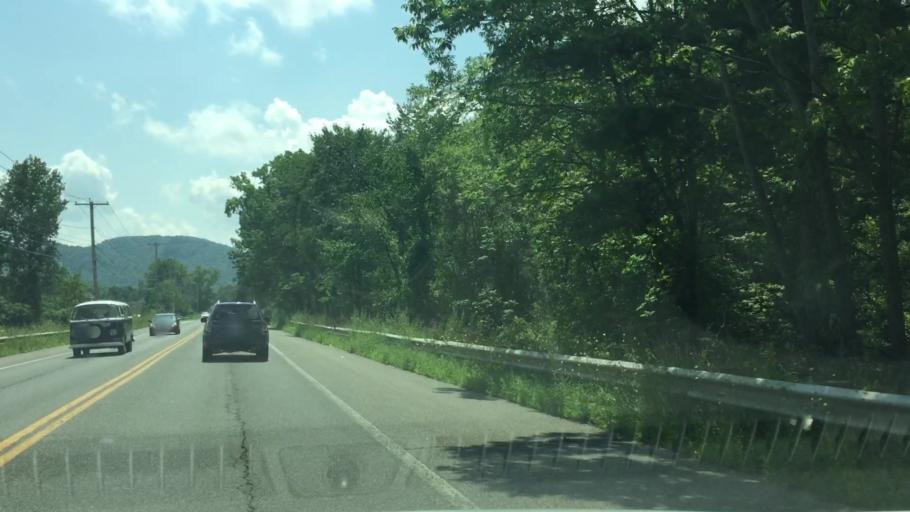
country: US
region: Massachusetts
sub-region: Berkshire County
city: Great Barrington
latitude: 42.2180
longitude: -73.3435
